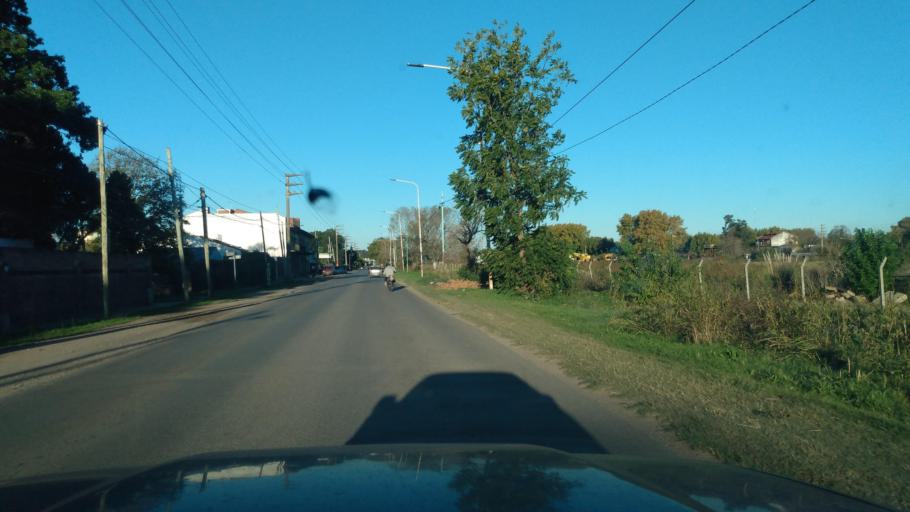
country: AR
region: Buenos Aires
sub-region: Partido de General Rodriguez
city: General Rodriguez
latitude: -34.6303
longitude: -58.8588
